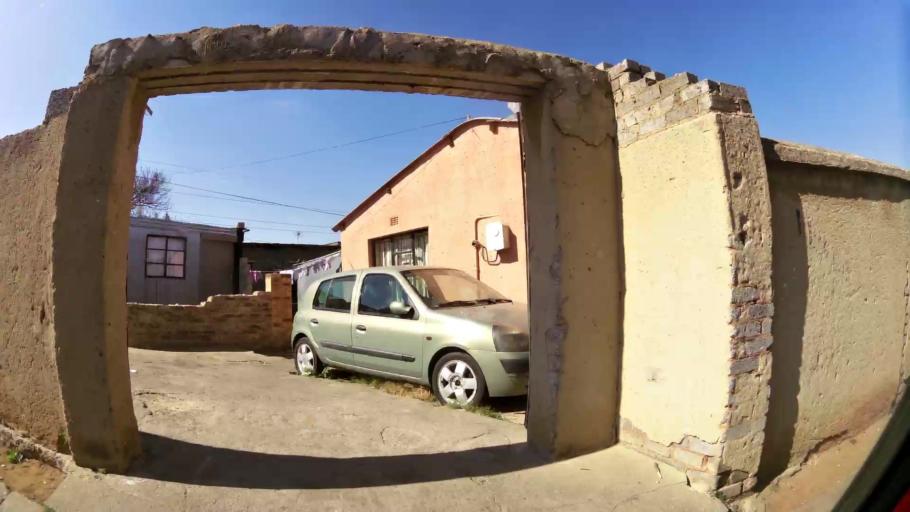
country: ZA
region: Gauteng
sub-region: City of Johannesburg Metropolitan Municipality
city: Soweto
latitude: -26.2440
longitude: 27.9005
